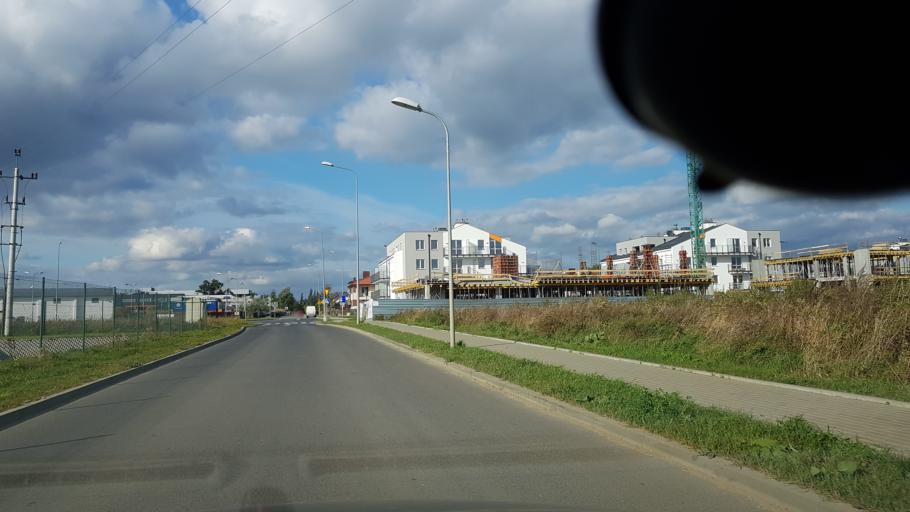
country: PL
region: Masovian Voivodeship
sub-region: Warszawa
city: Targowek
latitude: 52.3111
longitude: 21.0235
